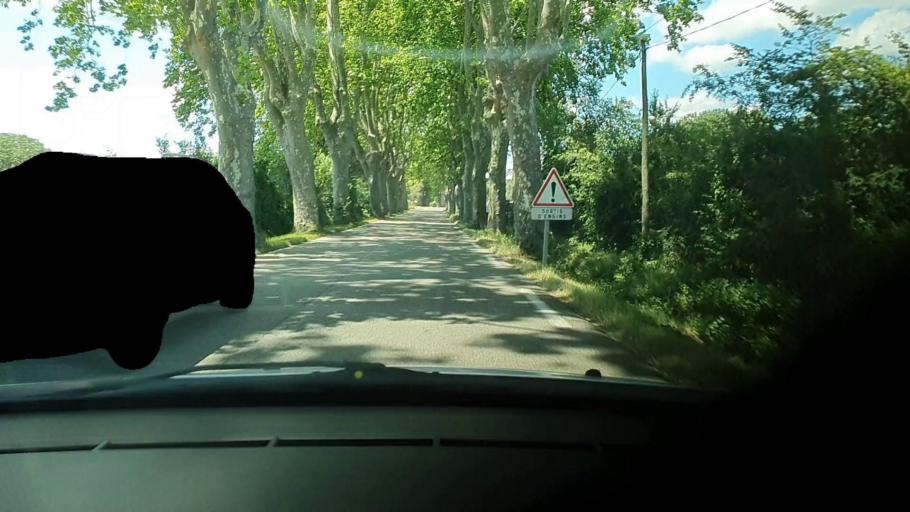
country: FR
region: Languedoc-Roussillon
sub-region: Departement du Gard
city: Montaren-et-Saint-Mediers
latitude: 44.0222
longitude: 4.3953
